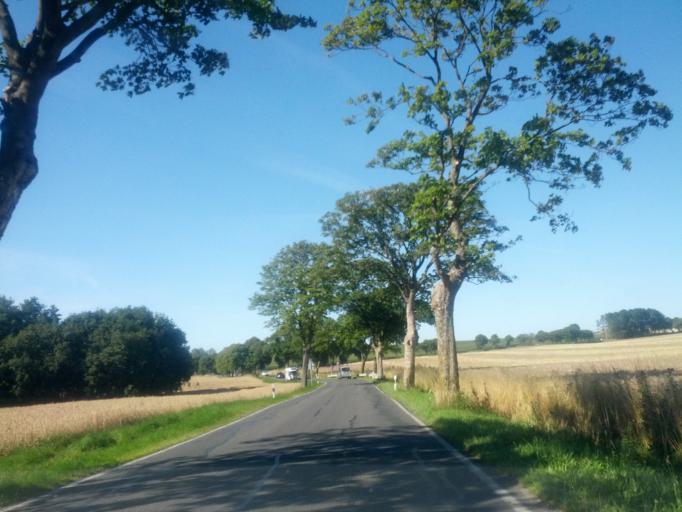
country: DE
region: Mecklenburg-Vorpommern
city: Bastorf
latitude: 54.1163
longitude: 11.6817
